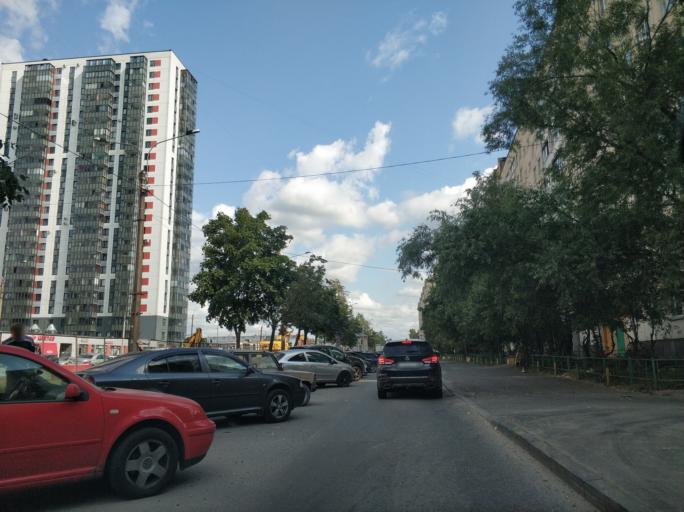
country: RU
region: St.-Petersburg
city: Krasnogvargeisky
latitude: 59.9592
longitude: 30.4806
